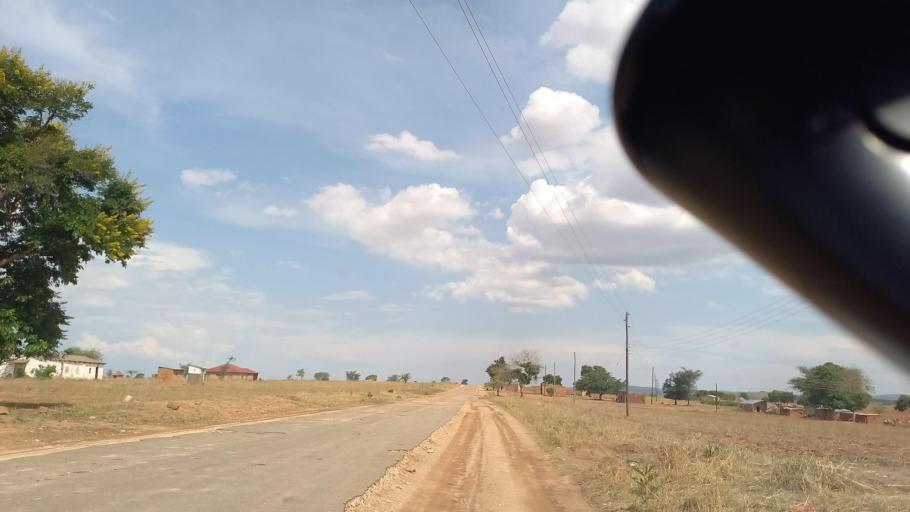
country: ZM
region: Lusaka
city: Kafue
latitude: -16.1922
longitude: 28.0929
